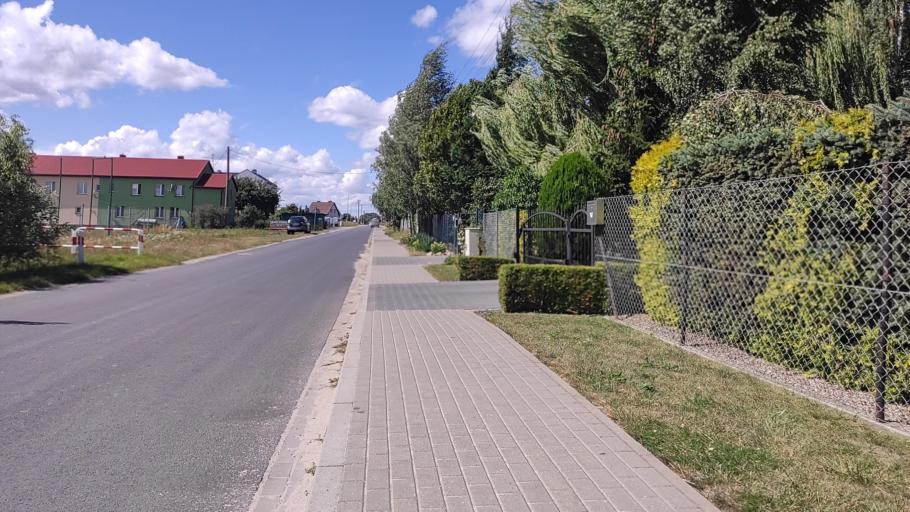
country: PL
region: Greater Poland Voivodeship
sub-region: Powiat poznanski
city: Kleszczewo
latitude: 52.3821
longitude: 17.1599
